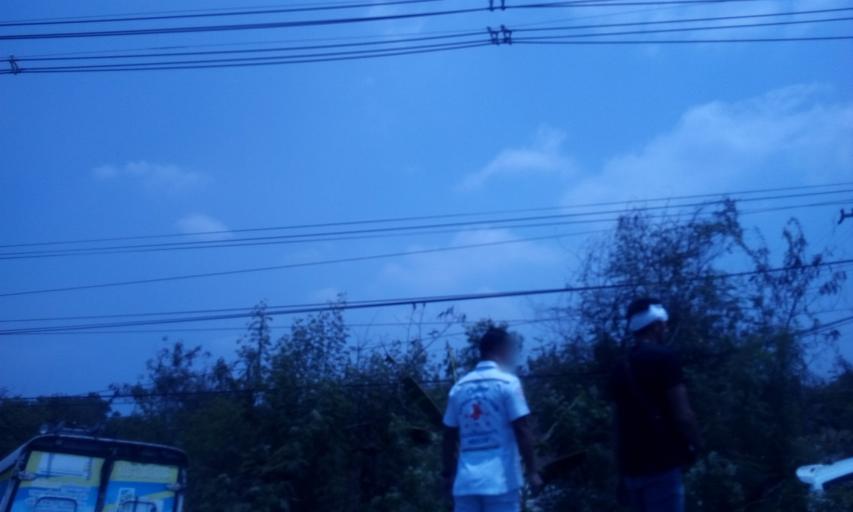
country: TH
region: Chachoengsao
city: Chachoengsao
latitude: 13.7326
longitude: 101.0873
